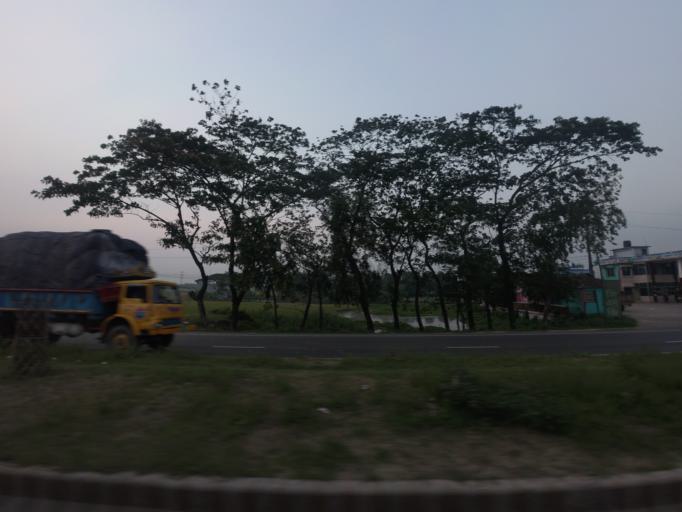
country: BD
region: Chittagong
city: Comilla
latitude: 23.4778
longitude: 91.1040
